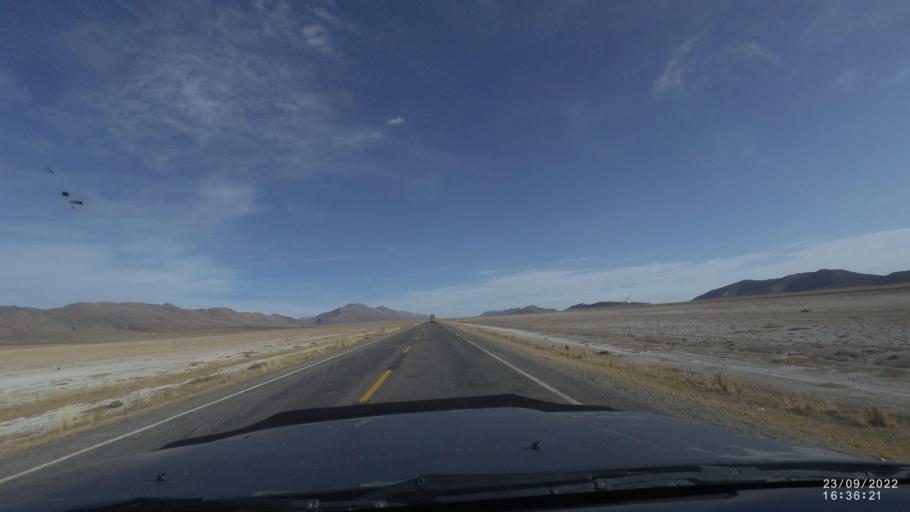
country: BO
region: Oruro
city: Machacamarca
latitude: -18.2184
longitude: -67.0082
